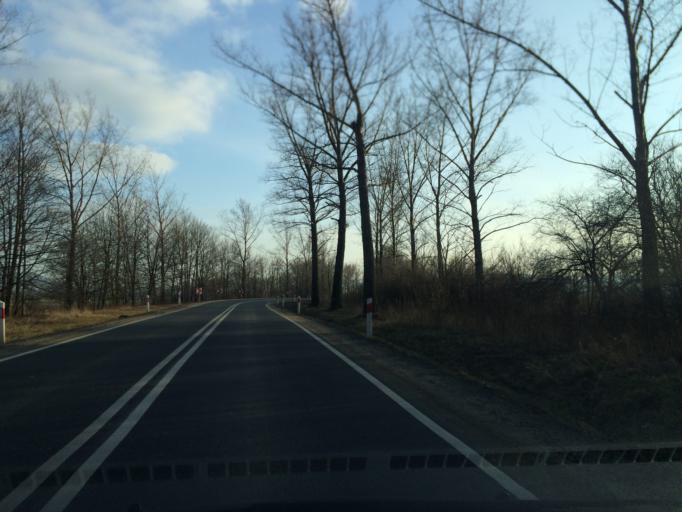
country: PL
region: Lower Silesian Voivodeship
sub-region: Powiat klodzki
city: Bystrzyca Klodzka
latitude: 50.2305
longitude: 16.6776
